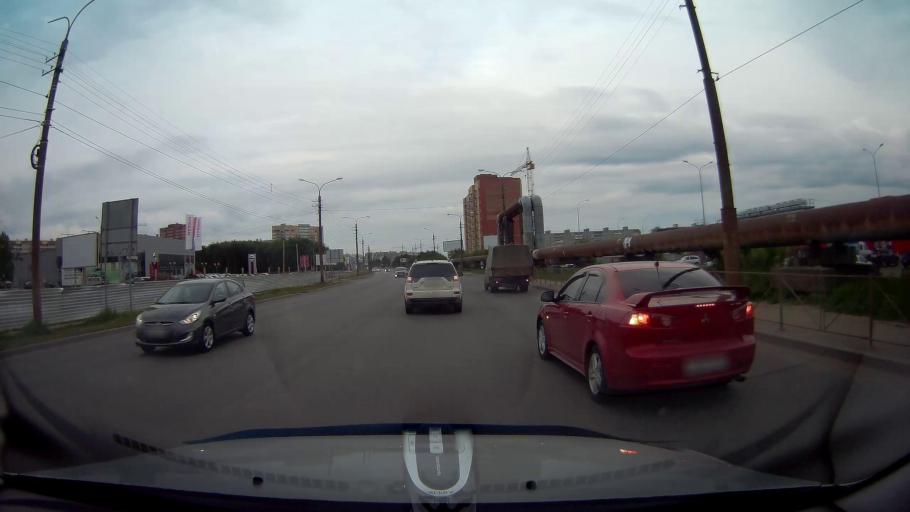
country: RU
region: Arkhangelskaya
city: Arkhangel'sk
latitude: 64.5319
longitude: 40.5983
